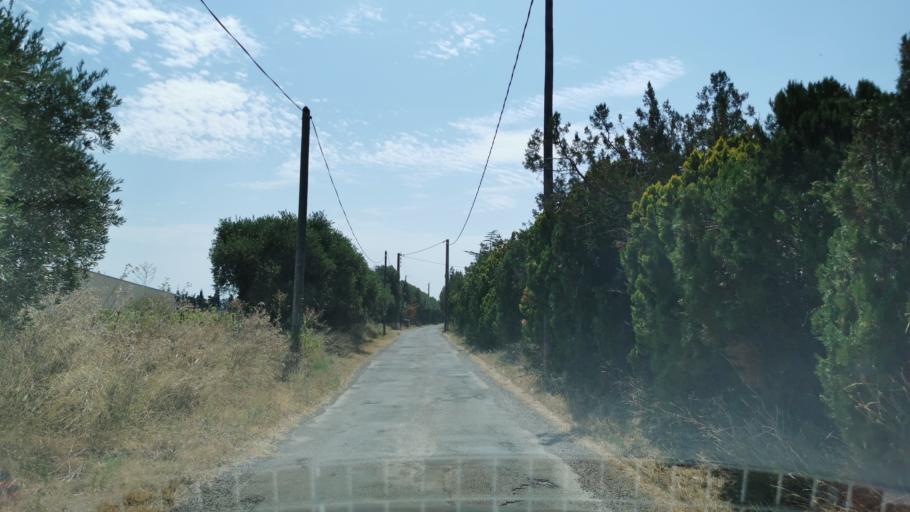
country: FR
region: Languedoc-Roussillon
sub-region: Departement de l'Aude
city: Bize-Minervois
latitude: 43.2954
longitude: 2.8809
